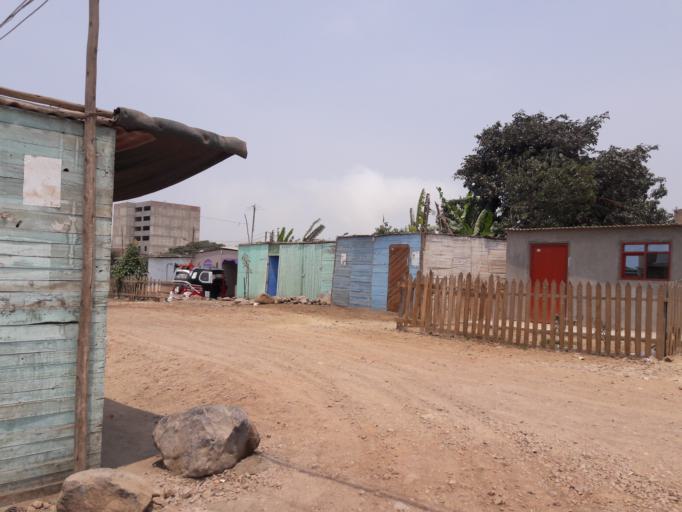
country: PE
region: Lima
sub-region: Lima
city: Santa Rosa
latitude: -11.7702
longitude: -77.1621
